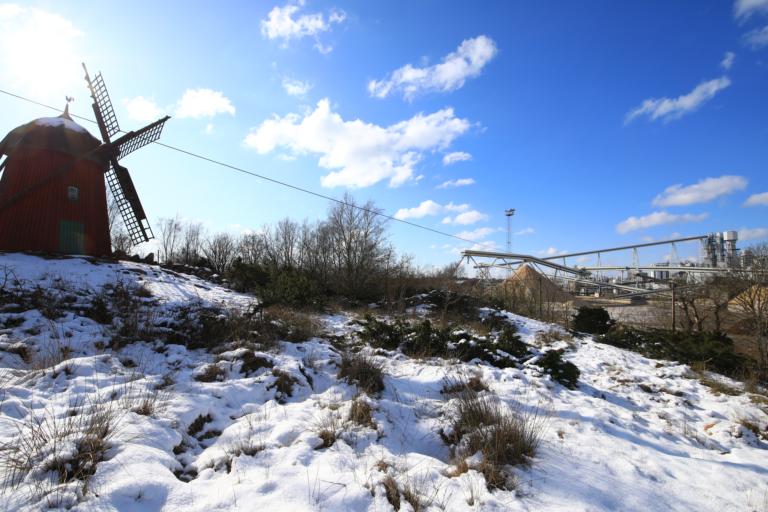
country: SE
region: Halland
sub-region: Kungsbacka Kommun
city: Frillesas
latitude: 57.2204
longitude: 12.1807
